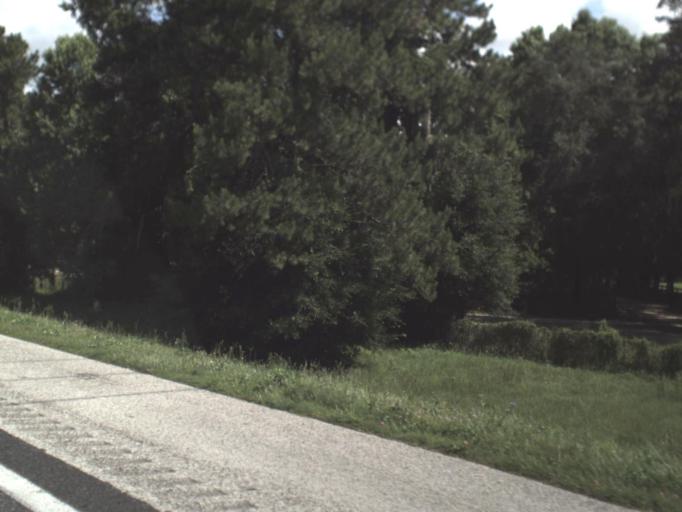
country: US
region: Florida
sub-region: Alachua County
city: Alachua
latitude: 29.7423
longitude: -82.4809
